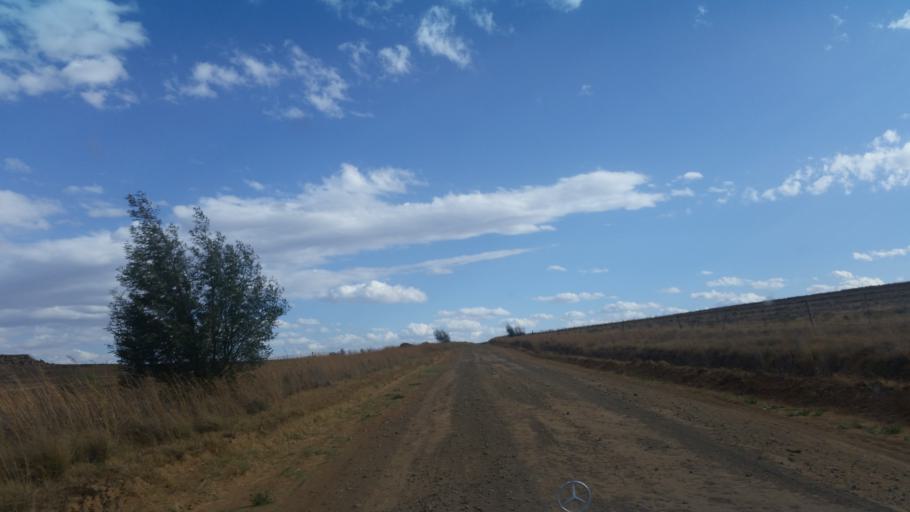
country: ZA
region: Orange Free State
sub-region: Thabo Mofutsanyana District Municipality
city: Phuthaditjhaba
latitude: -28.3534
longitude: 28.6036
